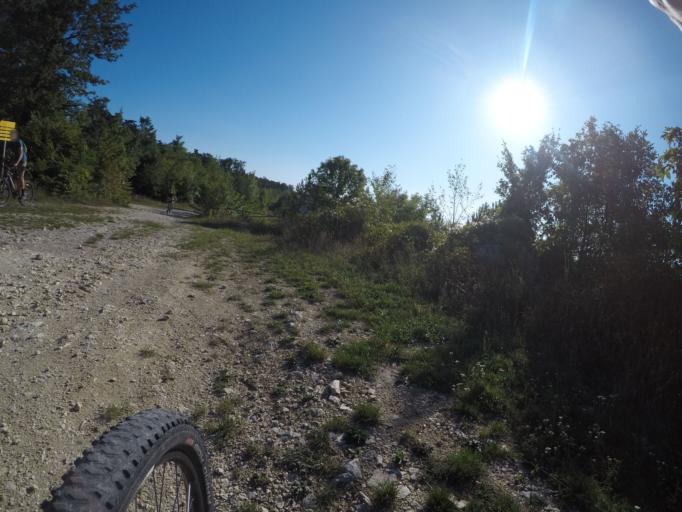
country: AT
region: Lower Austria
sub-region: Politischer Bezirk Bruck an der Leitha
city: Mannersdorf am Leithagebirge
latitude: 47.9646
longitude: 16.6127
